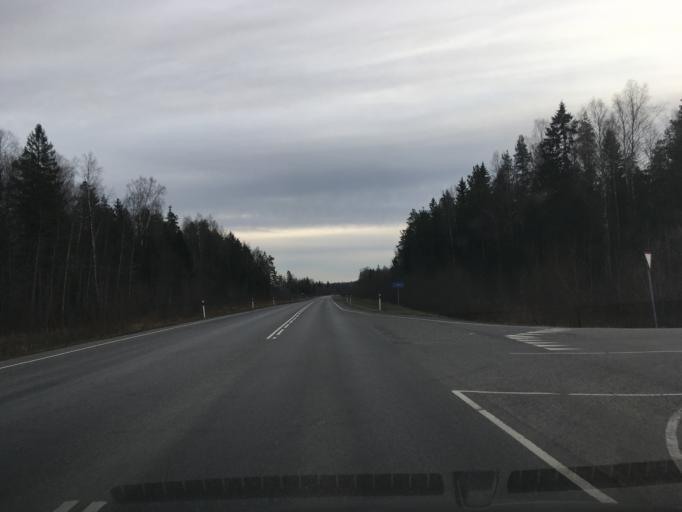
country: EE
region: Ida-Virumaa
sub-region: Johvi vald
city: Johvi
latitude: 59.3595
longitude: 27.4628
